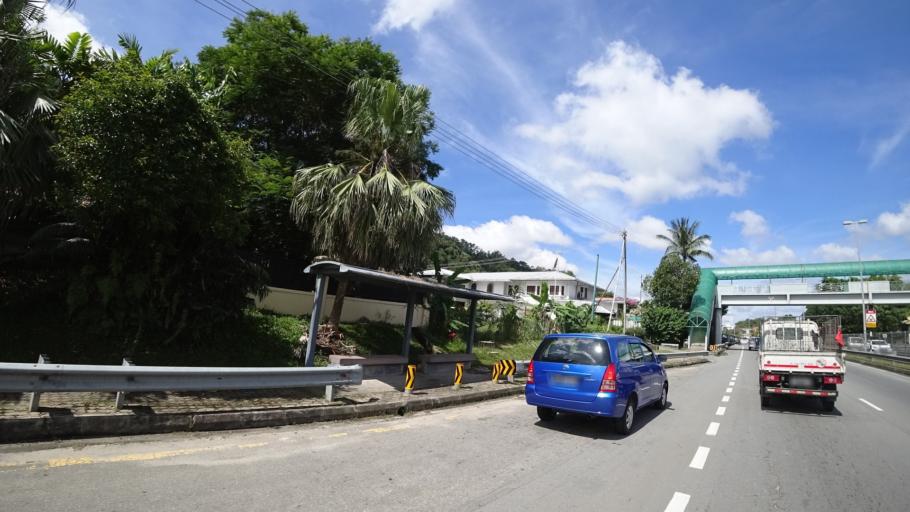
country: BN
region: Brunei and Muara
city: Bandar Seri Begawan
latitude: 4.8539
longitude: 114.8878
